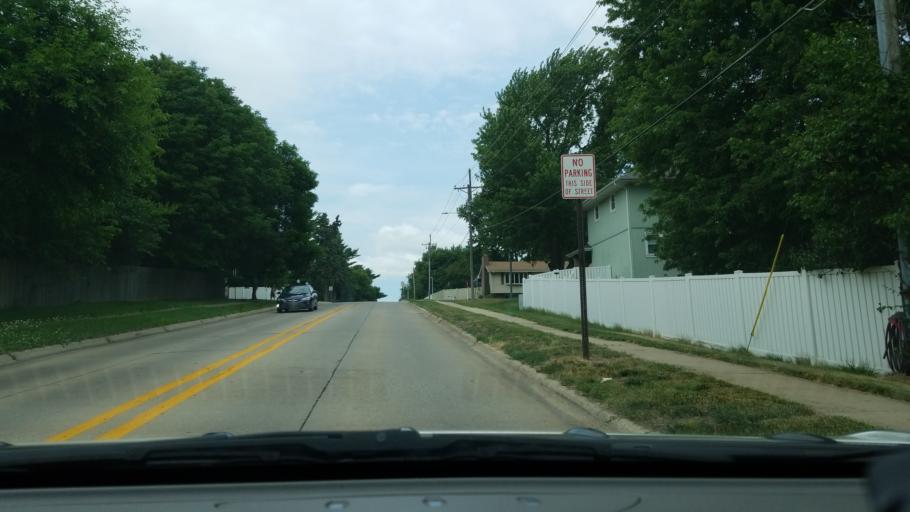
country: US
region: Nebraska
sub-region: Sarpy County
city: Papillion
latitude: 41.1436
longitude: -96.0283
